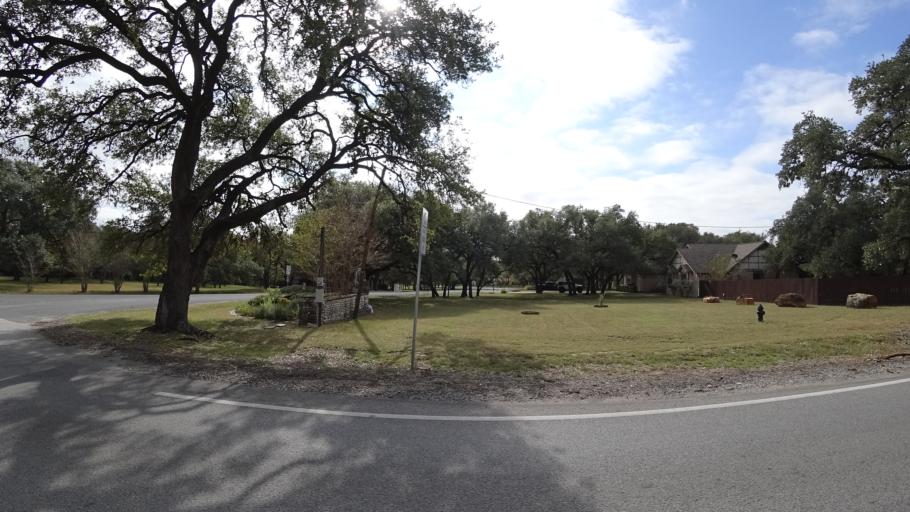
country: US
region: Texas
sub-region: Williamson County
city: Brushy Creek
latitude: 30.5319
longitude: -97.7277
